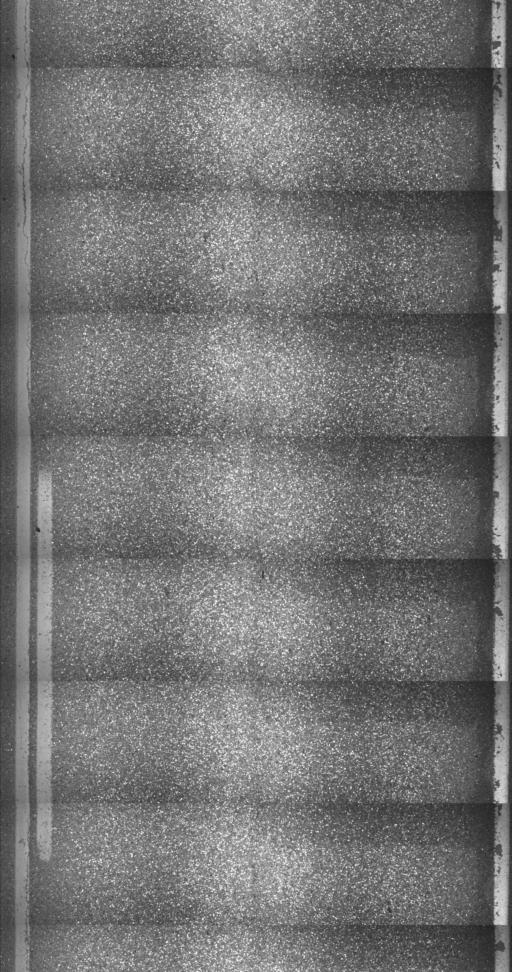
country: US
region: Vermont
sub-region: Washington County
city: Waterbury
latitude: 44.4325
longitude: -72.7136
